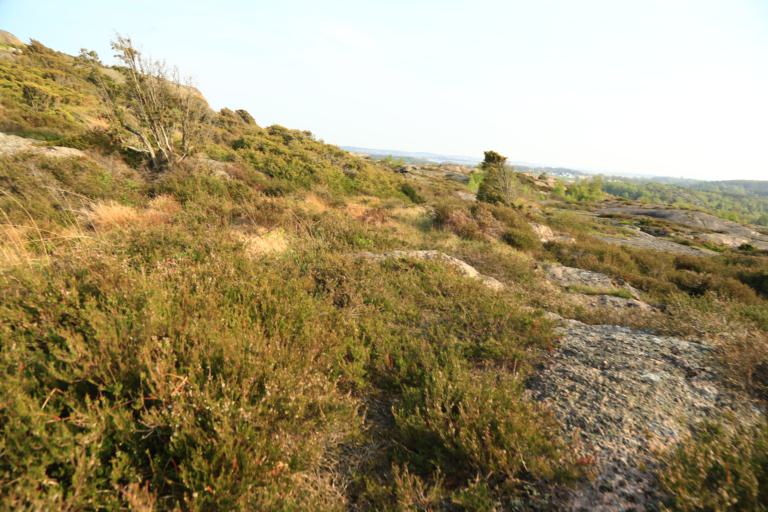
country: SE
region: Halland
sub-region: Varbergs Kommun
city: Varberg
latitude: 57.1584
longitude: 12.2336
